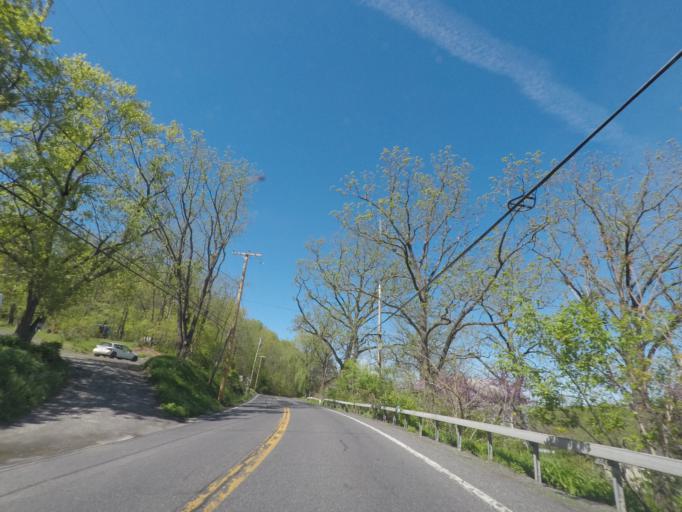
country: US
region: New York
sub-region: Ulster County
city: Saugerties
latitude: 42.1253
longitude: -73.9303
